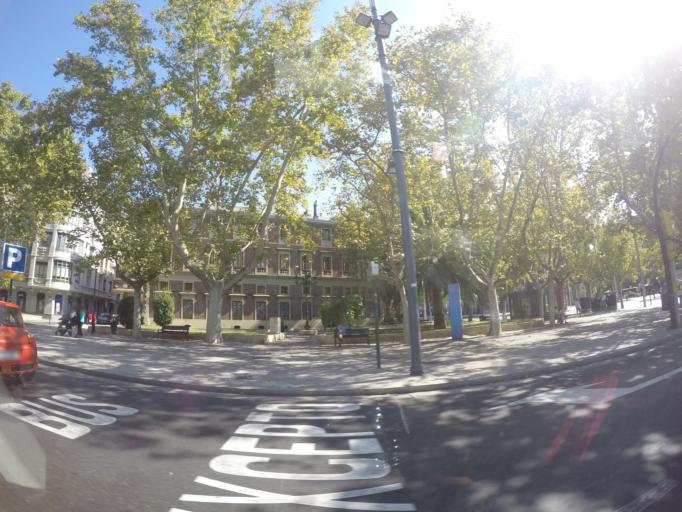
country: ES
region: Aragon
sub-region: Provincia de Zaragoza
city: Zaragoza
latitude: 41.6478
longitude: -0.8863
